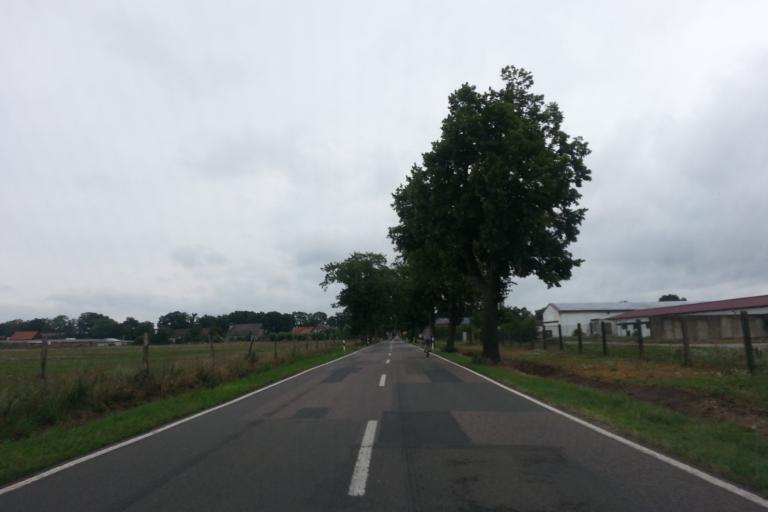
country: DE
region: Mecklenburg-Vorpommern
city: Ferdinandshof
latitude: 53.6784
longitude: 13.9155
